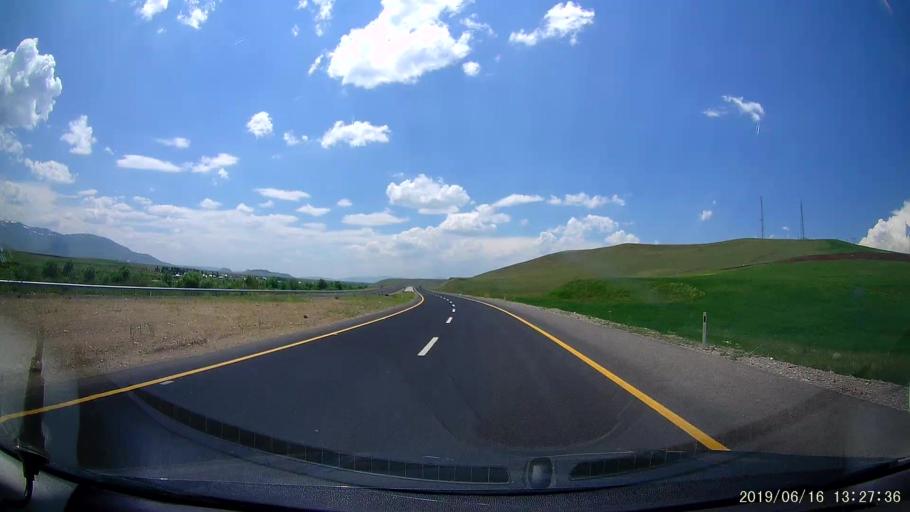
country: TR
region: Agri
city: Murat
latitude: 39.6718
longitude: 43.3069
